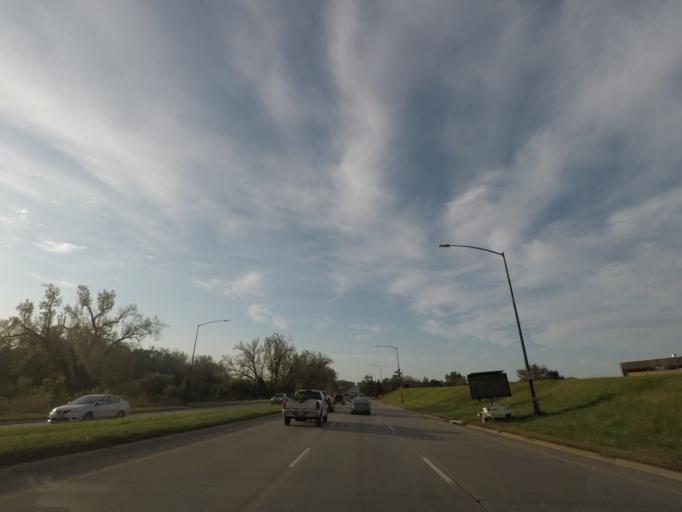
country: US
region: Iowa
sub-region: Polk County
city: Des Moines
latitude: 41.5780
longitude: -93.6450
